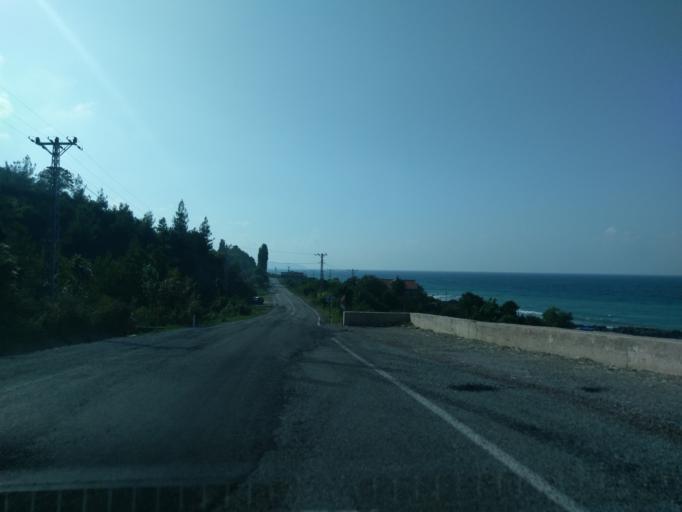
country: TR
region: Sinop
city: Ayancik
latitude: 41.9407
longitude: 34.6583
